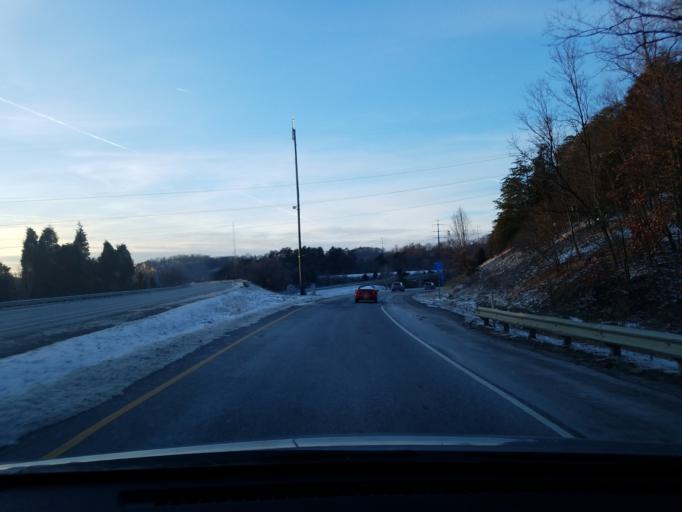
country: US
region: Indiana
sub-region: Floyd County
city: New Albany
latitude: 38.3012
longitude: -85.8482
